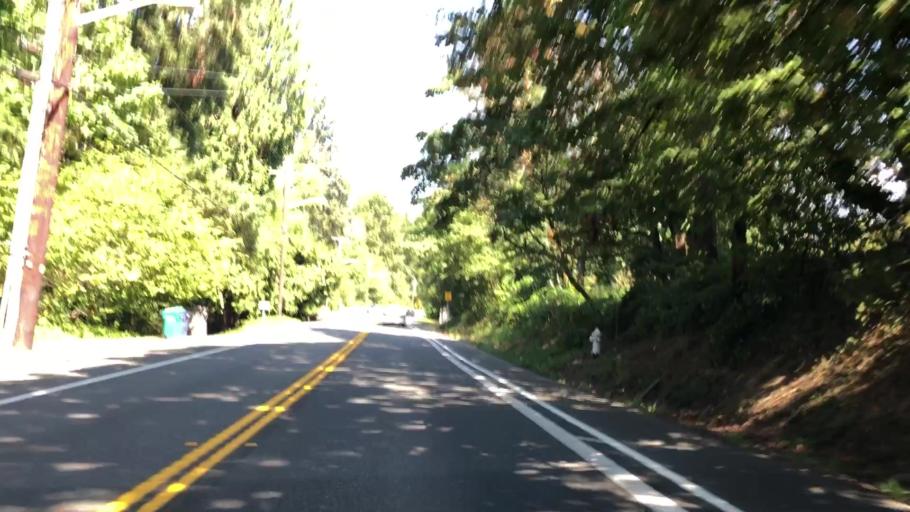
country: US
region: Washington
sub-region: King County
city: Inglewood-Finn Hill
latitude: 47.7161
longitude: -122.2362
